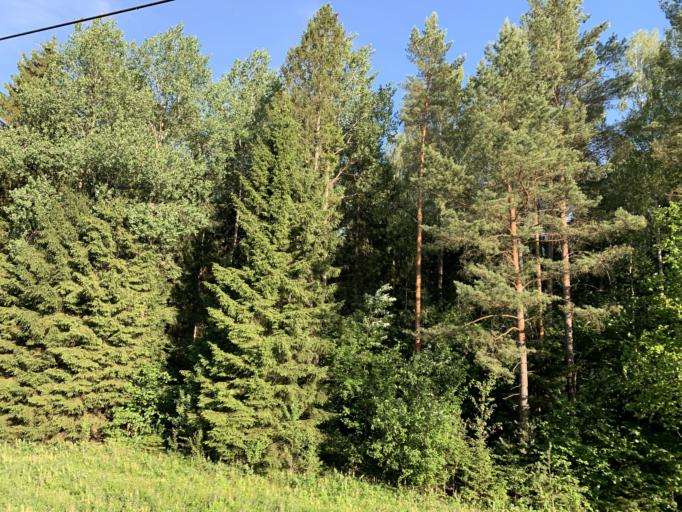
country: BY
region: Minsk
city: Enyerhyetykaw
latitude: 53.5237
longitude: 26.9070
